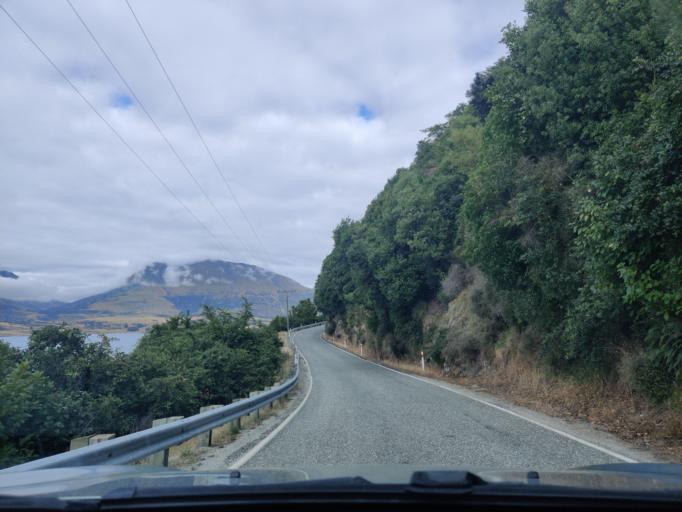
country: NZ
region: Otago
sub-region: Queenstown-Lakes District
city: Queenstown
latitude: -45.0799
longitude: 168.4804
